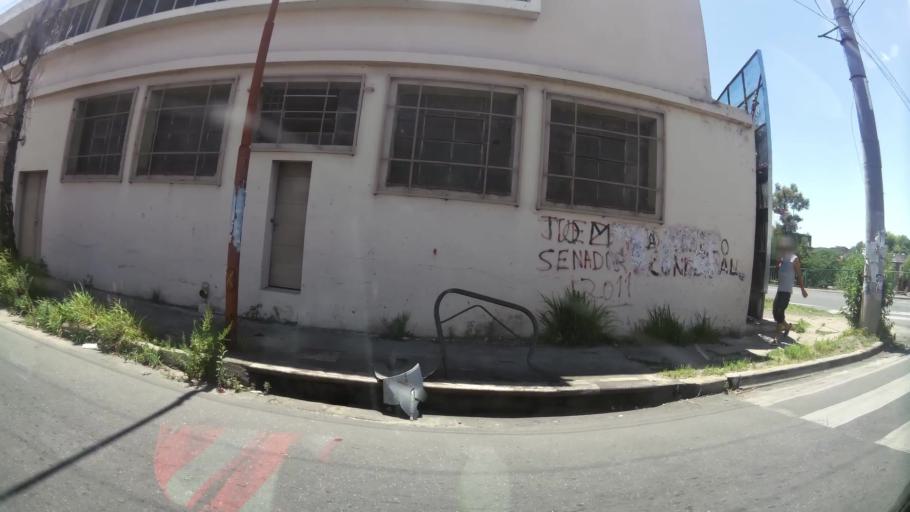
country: AR
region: Cordoba
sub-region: Departamento de Capital
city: Cordoba
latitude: -31.3966
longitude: -64.2033
